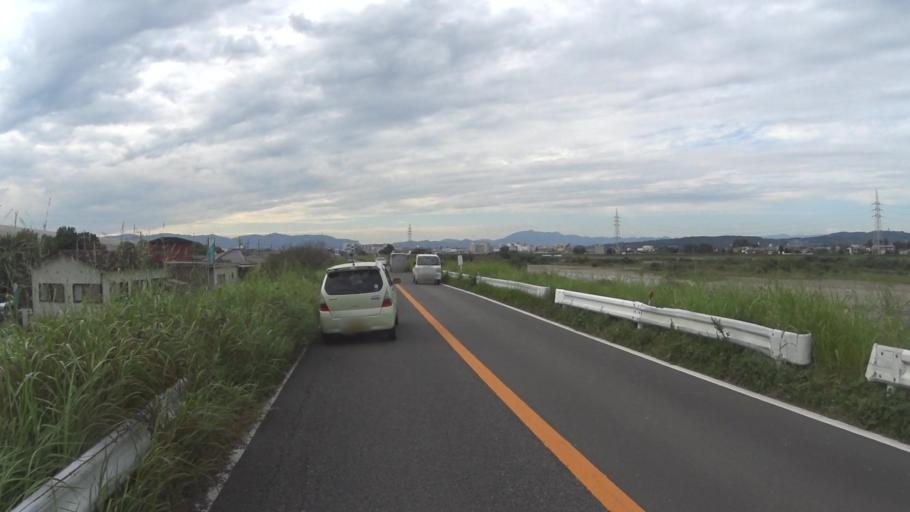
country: JP
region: Kyoto
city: Uji
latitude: 34.9038
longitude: 135.7962
